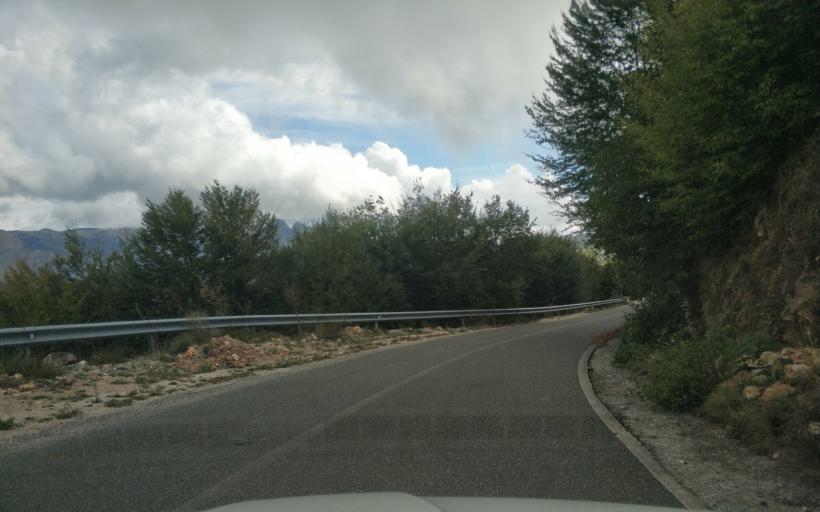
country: AL
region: Durres
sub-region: Rrethi i Krujes
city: Kruje
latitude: 41.5194
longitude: 19.8028
